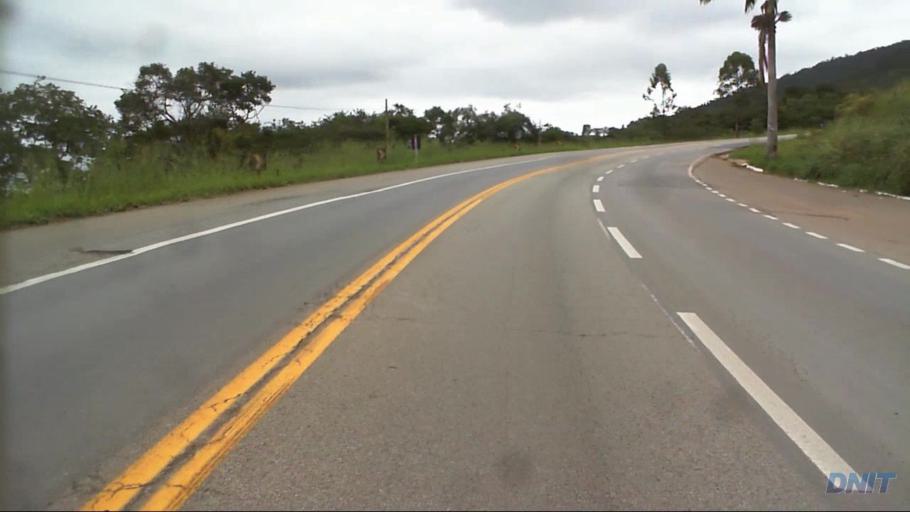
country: BR
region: Minas Gerais
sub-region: Barao De Cocais
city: Barao de Cocais
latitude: -19.7389
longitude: -43.5152
